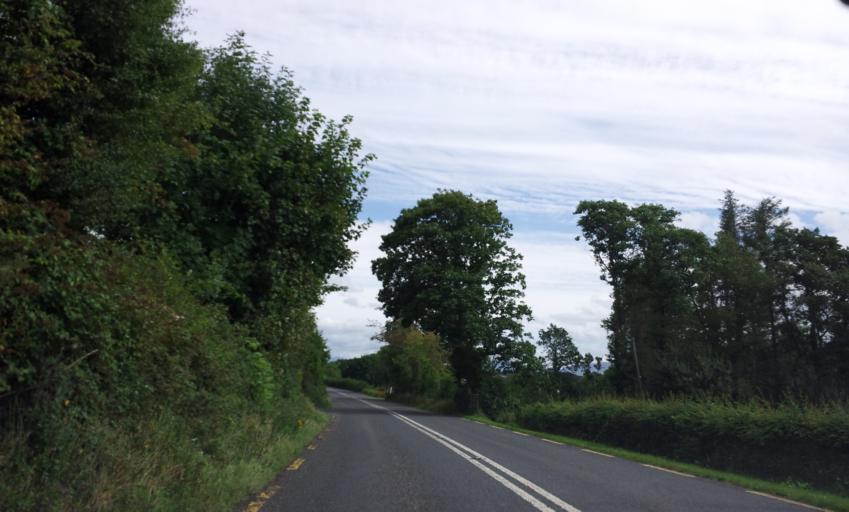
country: IE
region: Munster
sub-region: Ciarrai
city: Killorglin
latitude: 52.0763
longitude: -9.6547
